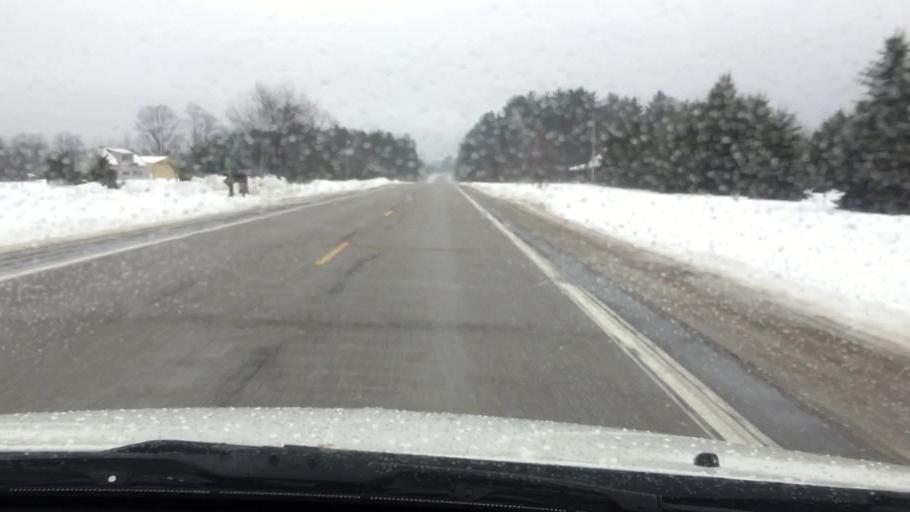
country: US
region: Michigan
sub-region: Charlevoix County
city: East Jordan
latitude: 45.0988
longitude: -85.1100
